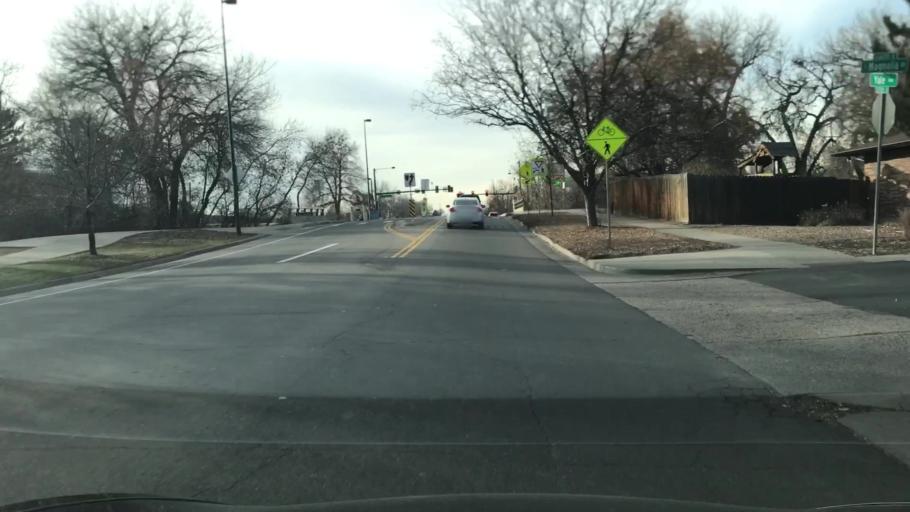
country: US
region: Colorado
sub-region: Arapahoe County
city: Glendale
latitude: 39.6677
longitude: -104.9109
